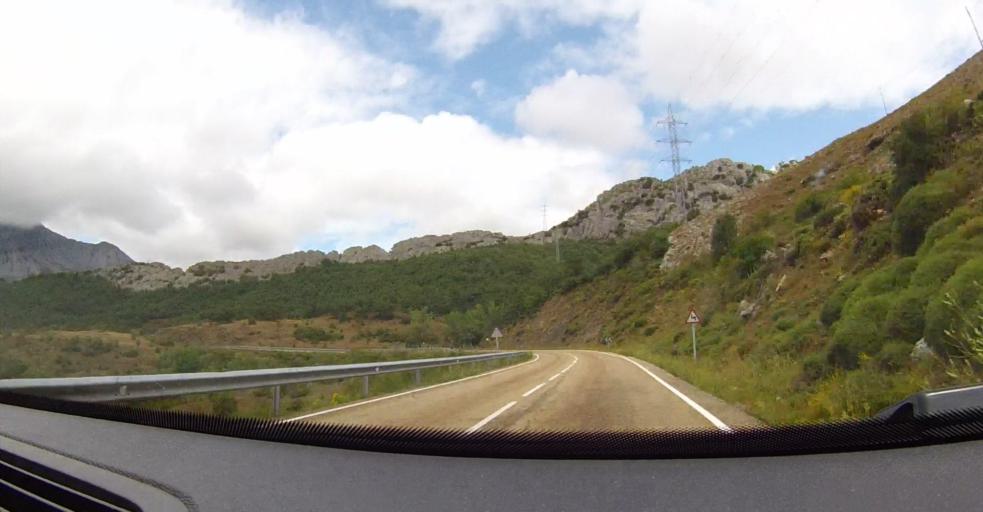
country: ES
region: Castille and Leon
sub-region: Provincia de Leon
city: Puebla de Lillo
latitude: 42.9656
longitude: -5.2548
